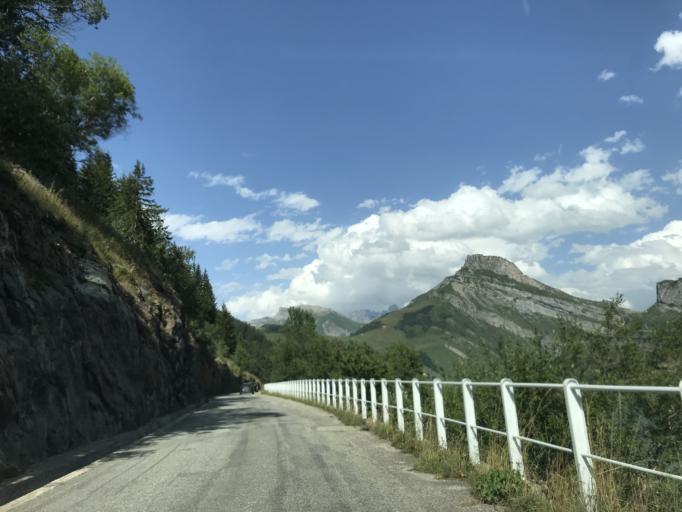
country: FR
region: Rhone-Alpes
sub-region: Departement de la Savoie
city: Beaufort
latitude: 45.6893
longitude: 6.6273
